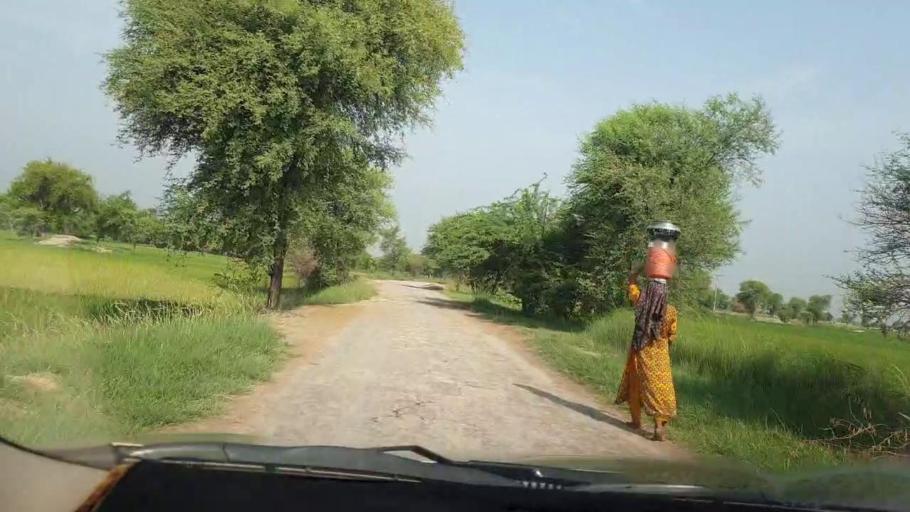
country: PK
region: Sindh
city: Goth Garelo
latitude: 27.4508
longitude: 68.0210
